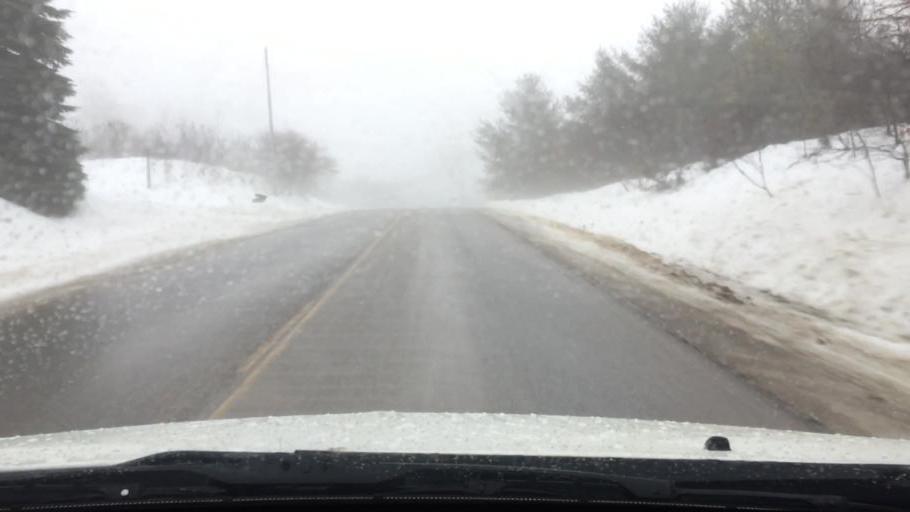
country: US
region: Michigan
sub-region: Charlevoix County
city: East Jordan
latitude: 45.1248
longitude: -85.1802
